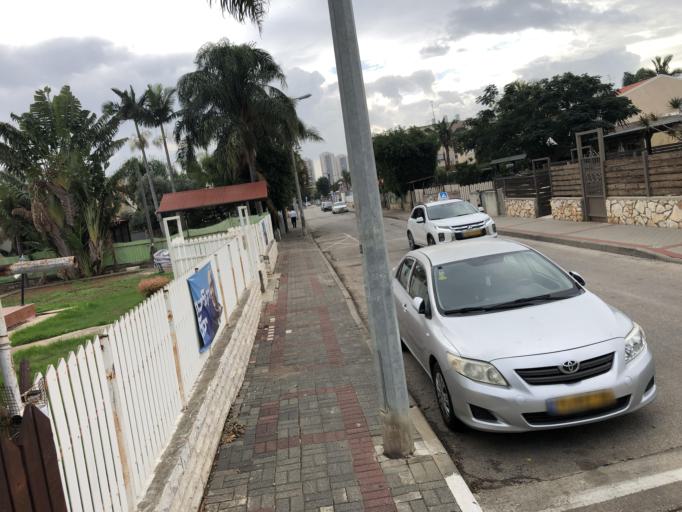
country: IL
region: Northern District
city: `Akko
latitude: 32.9291
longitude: 35.0944
